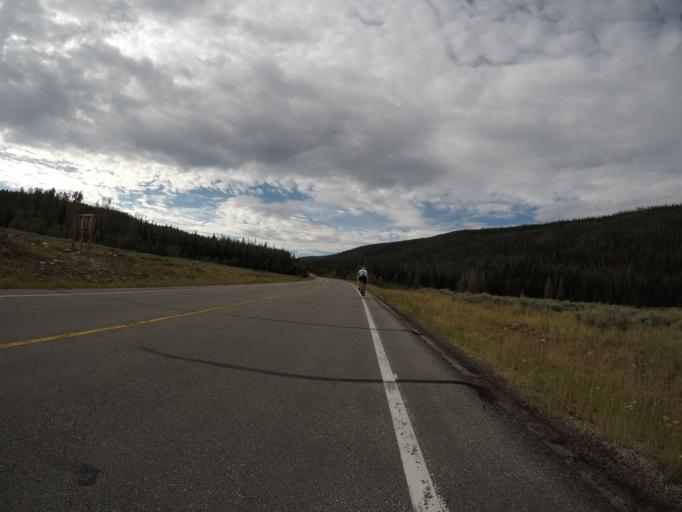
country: US
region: Wyoming
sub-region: Carbon County
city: Saratoga
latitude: 41.3419
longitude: -106.5262
